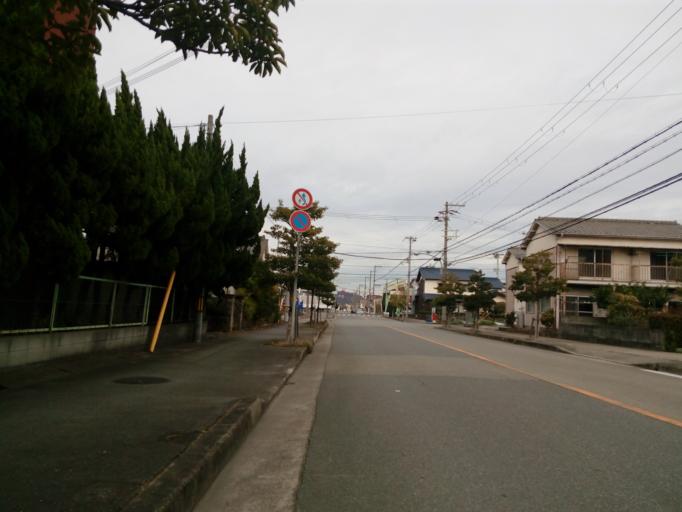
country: JP
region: Hyogo
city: Tatsunocho-tominaga
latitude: 34.7900
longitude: 134.6086
